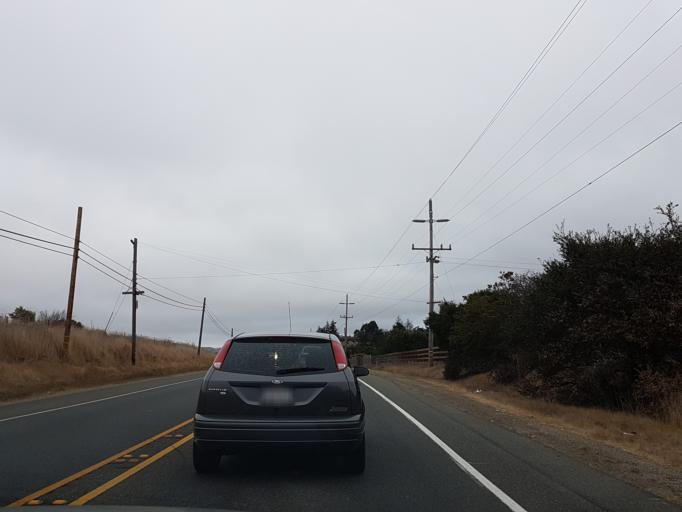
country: US
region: California
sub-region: Monterey County
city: Carmel Valley Village
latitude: 36.5730
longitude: -121.7382
